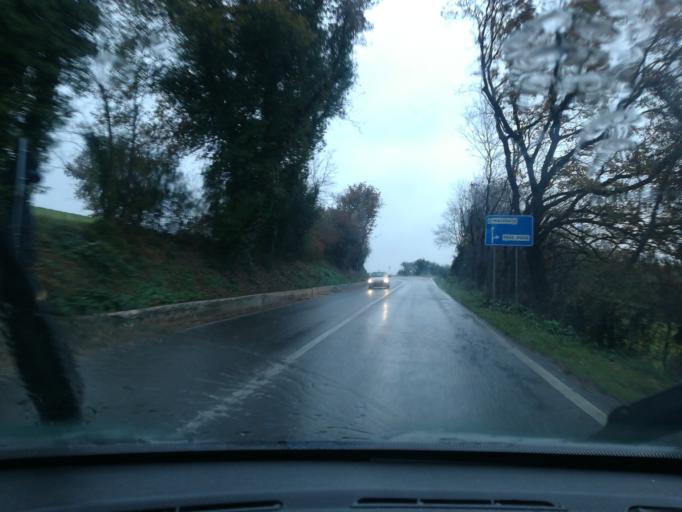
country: IT
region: The Marches
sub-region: Provincia di Macerata
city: Sforzacosta
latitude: 43.2747
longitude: 13.4303
